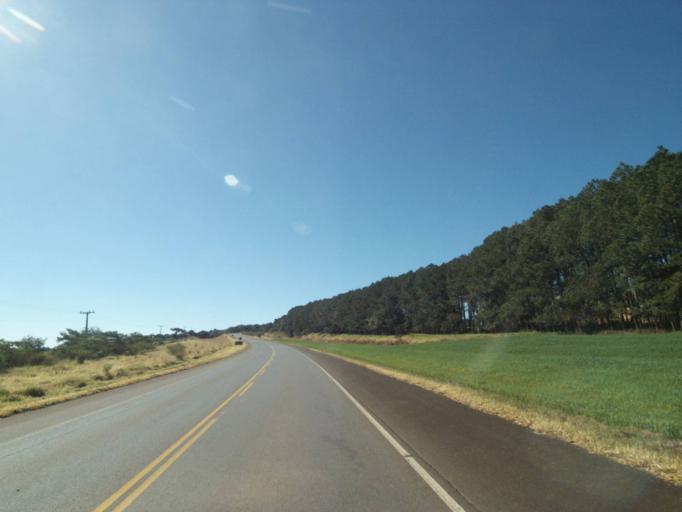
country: BR
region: Parana
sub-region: Tibagi
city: Tibagi
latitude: -24.4154
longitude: -50.3664
